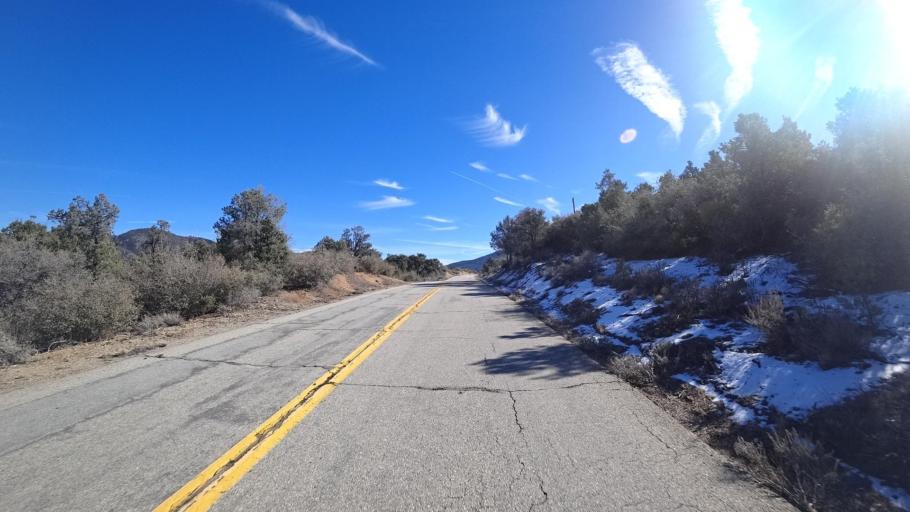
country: US
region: California
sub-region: Kern County
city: Pine Mountain Club
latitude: 34.8712
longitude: -119.2672
